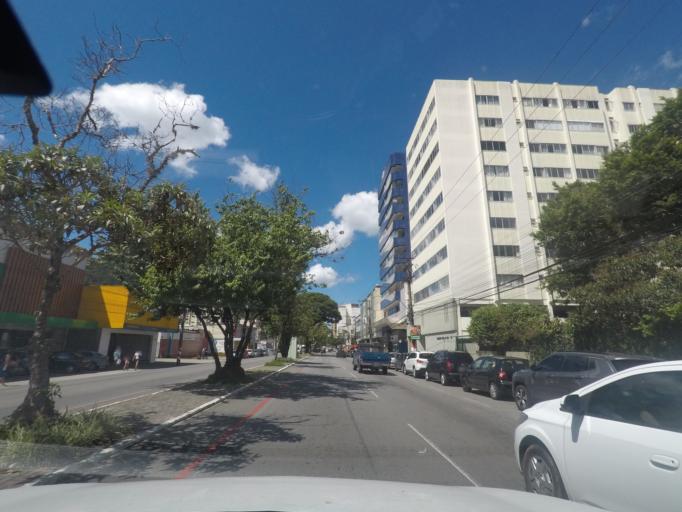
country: BR
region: Rio de Janeiro
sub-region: Teresopolis
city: Teresopolis
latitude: -22.4202
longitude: -42.9750
